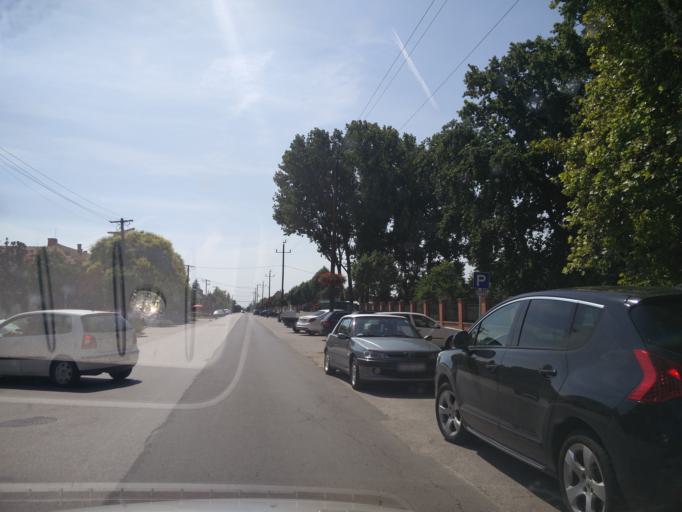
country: HU
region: Csongrad
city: Sandorfalva
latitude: 46.3608
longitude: 20.0991
